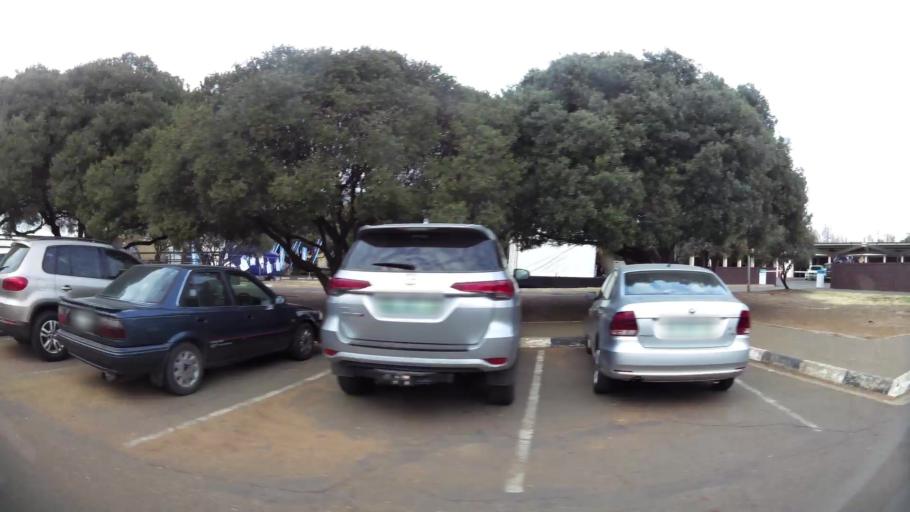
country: ZA
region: Orange Free State
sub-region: Mangaung Metropolitan Municipality
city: Bloemfontein
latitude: -29.1122
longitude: 26.1894
